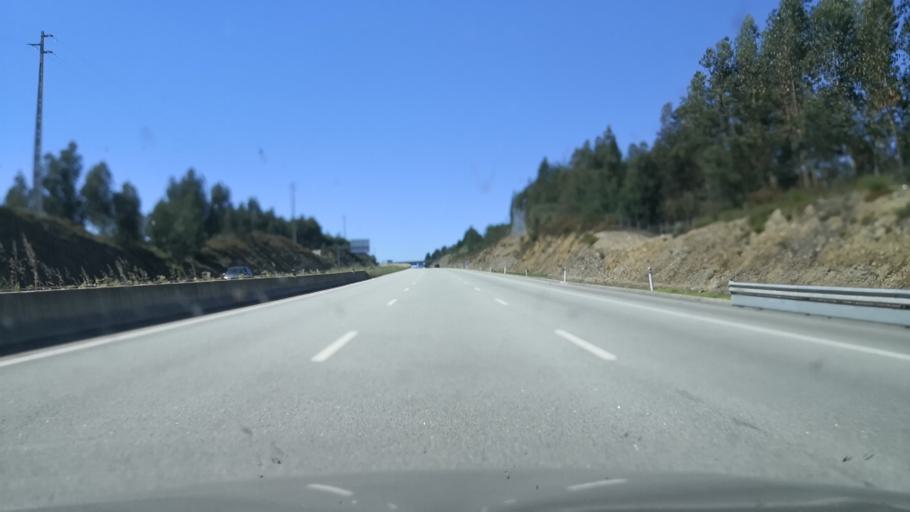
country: PT
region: Porto
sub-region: Gondomar
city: Foz do Sousa
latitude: 41.0832
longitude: -8.4538
